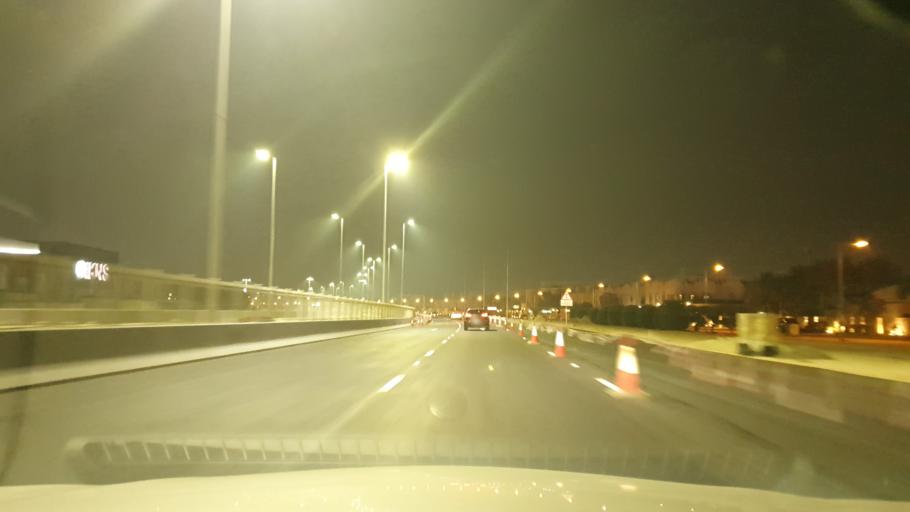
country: BH
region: Northern
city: Madinat `Isa
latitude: 26.1572
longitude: 50.5523
